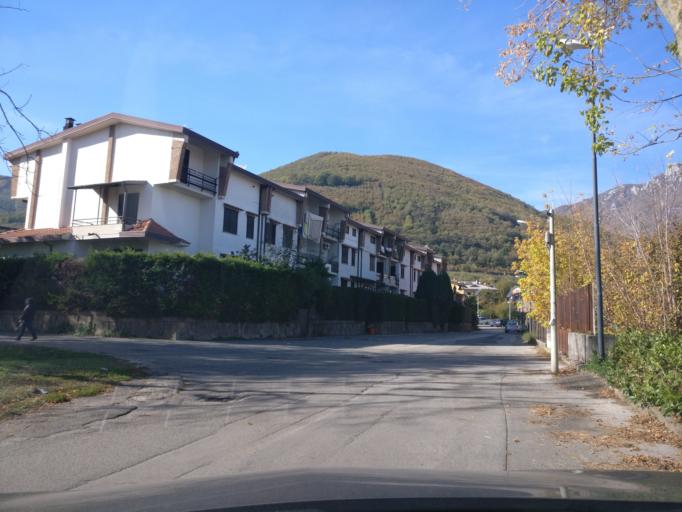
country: IT
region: Campania
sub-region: Provincia di Avellino
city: Monteforte Irpino
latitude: 40.9018
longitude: 14.7452
